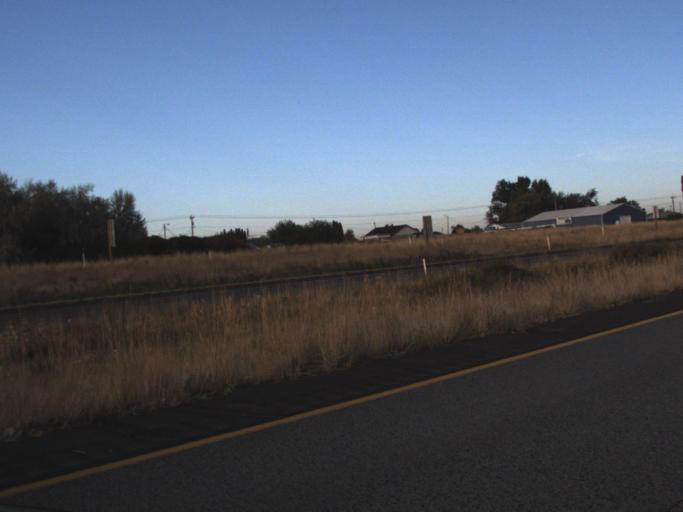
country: US
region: Washington
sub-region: Benton County
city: Prosser
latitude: 46.2232
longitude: -119.7931
